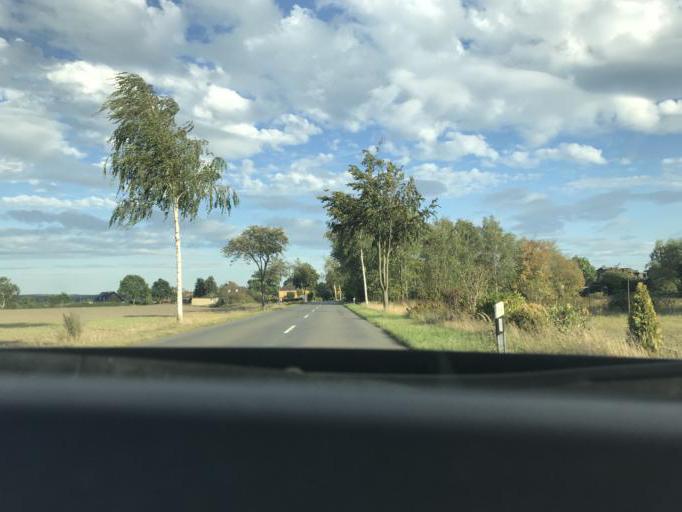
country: DE
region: Lower Saxony
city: Stadensen
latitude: 52.8794
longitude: 10.5464
